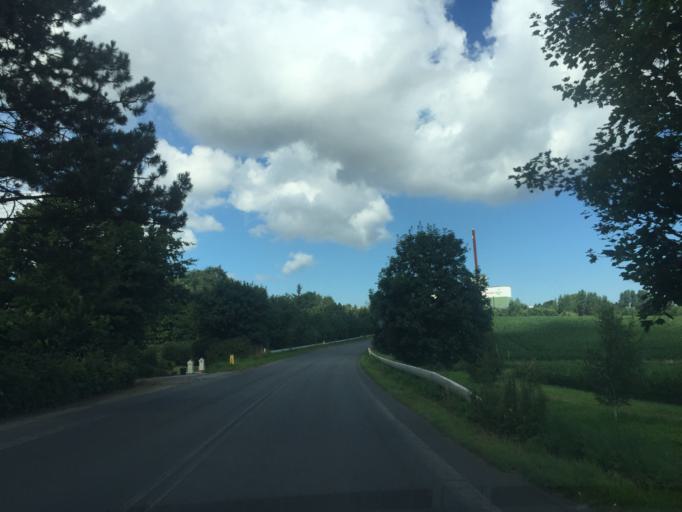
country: DK
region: South Denmark
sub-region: Nordfyns Kommune
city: Otterup
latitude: 55.5318
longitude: 10.3874
